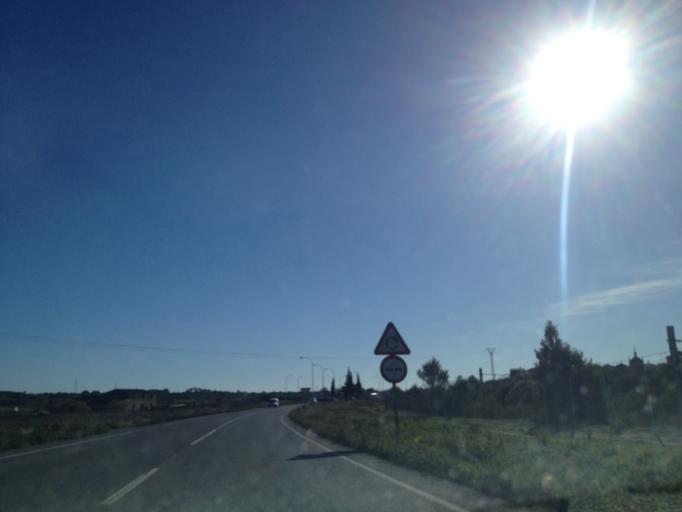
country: ES
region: Balearic Islands
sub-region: Illes Balears
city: Petra
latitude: 39.6187
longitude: 3.1195
